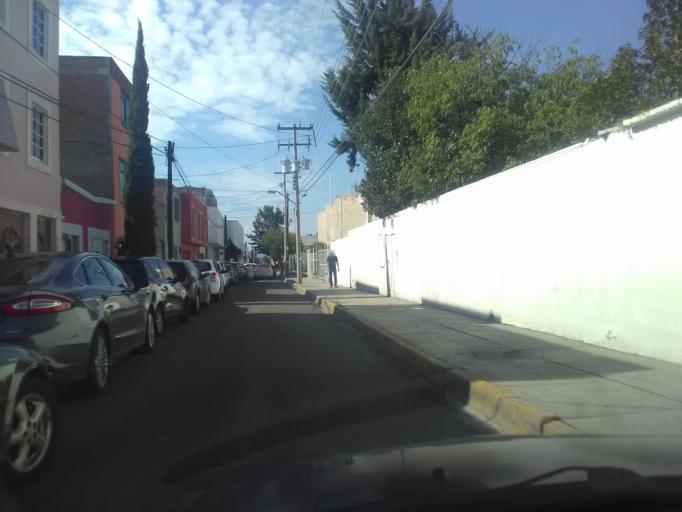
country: MX
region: Durango
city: Victoria de Durango
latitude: 24.0274
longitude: -104.6590
